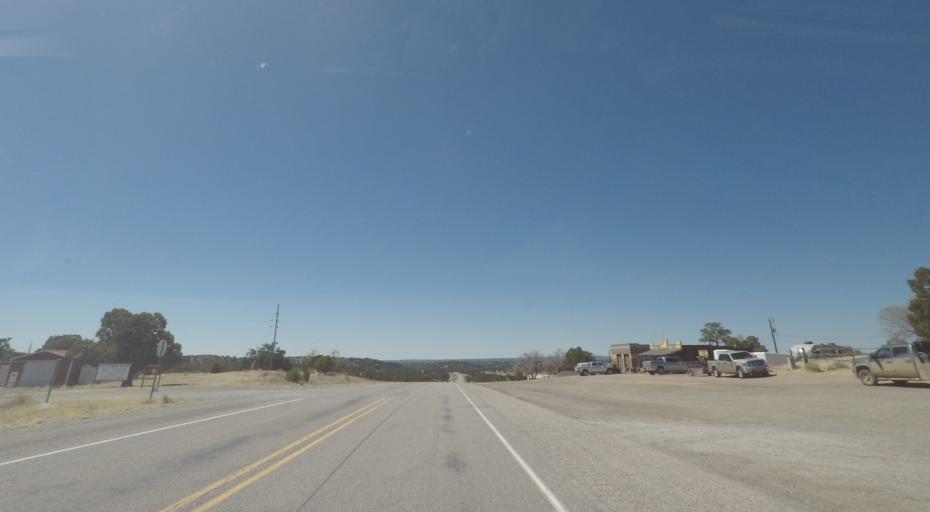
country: US
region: New Mexico
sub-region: Socorro County
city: Alamo
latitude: 34.2994
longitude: -108.1323
